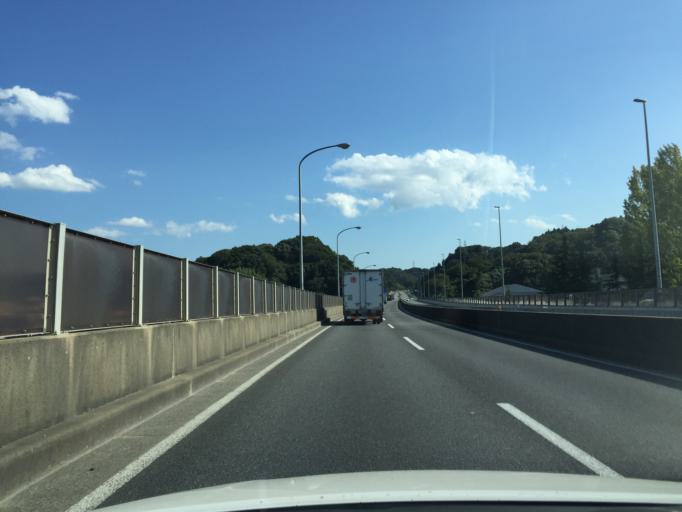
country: JP
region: Fukushima
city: Iwaki
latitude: 37.0482
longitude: 140.8692
